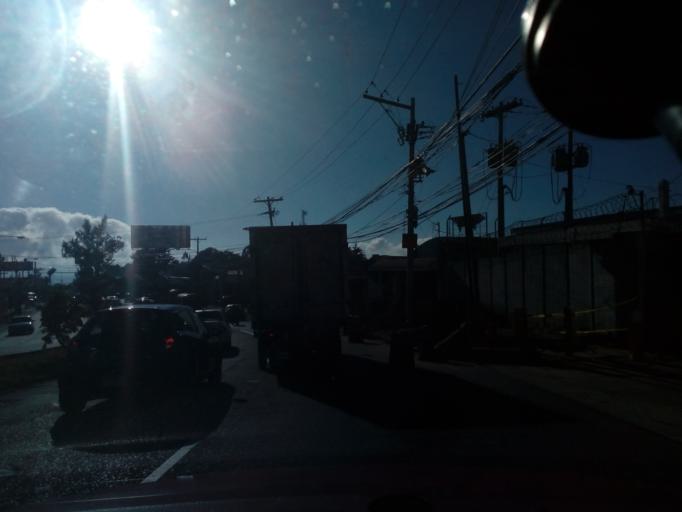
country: GT
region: Guatemala
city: Mixco
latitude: 14.6142
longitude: -90.6052
